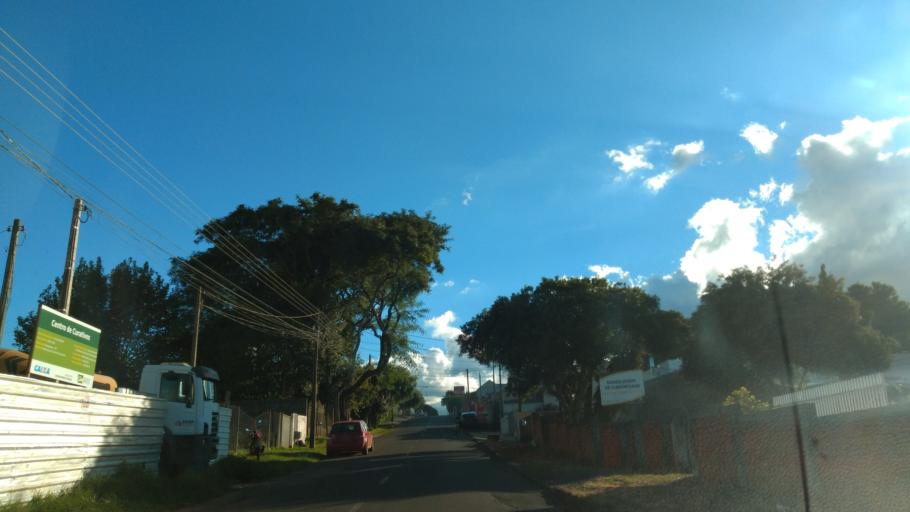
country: BR
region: Parana
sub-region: Guarapuava
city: Guarapuava
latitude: -25.3834
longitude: -51.4585
